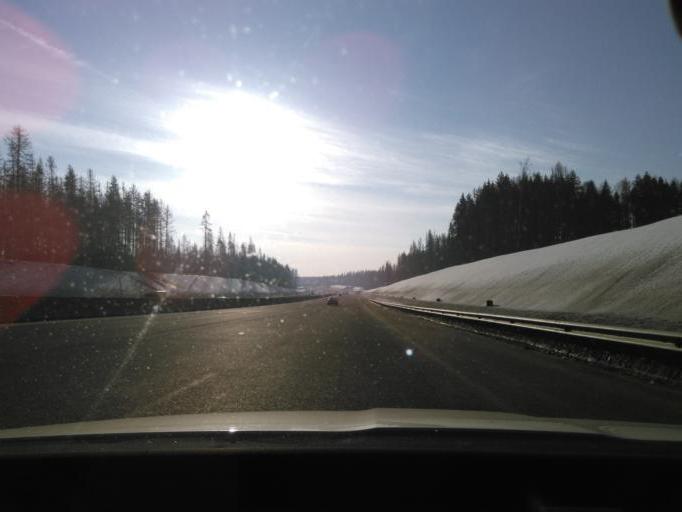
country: RU
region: Moskovskaya
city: Skhodnya
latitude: 55.9828
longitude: 37.3112
